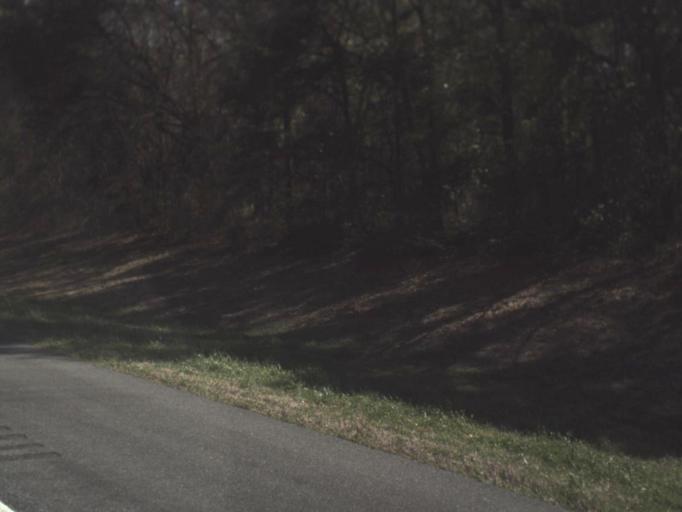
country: US
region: Florida
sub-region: Jackson County
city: Marianna
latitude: 30.6962
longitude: -85.1281
